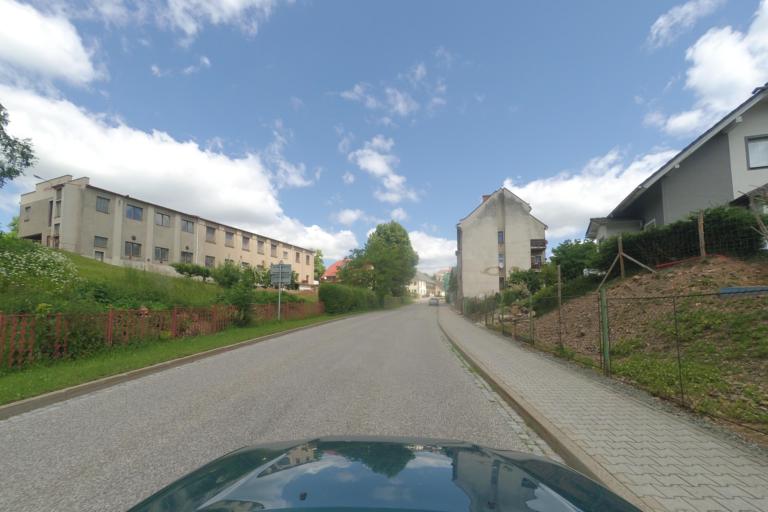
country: PL
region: Lower Silesian Voivodeship
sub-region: Powiat klodzki
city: Lewin Klodzki
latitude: 50.3562
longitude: 16.2446
